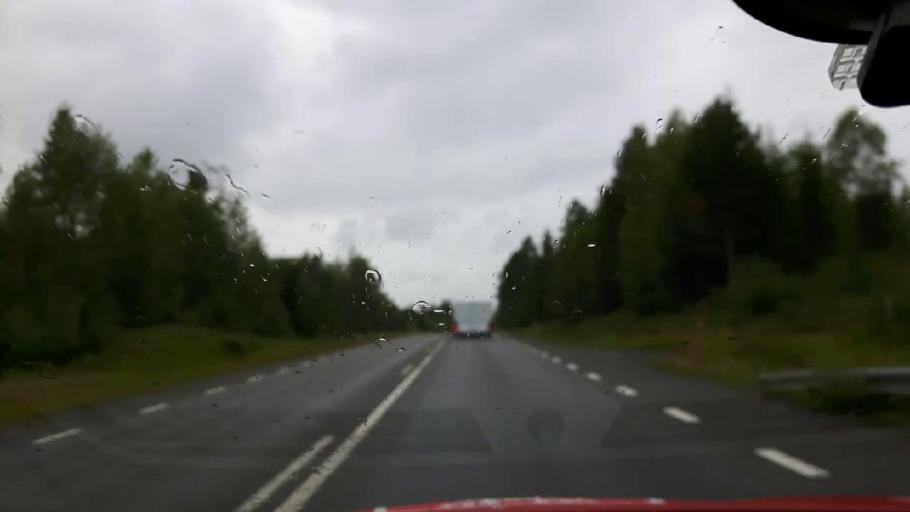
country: SE
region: Jaemtland
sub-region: Are Kommun
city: Jarpen
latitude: 63.3188
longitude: 13.5671
